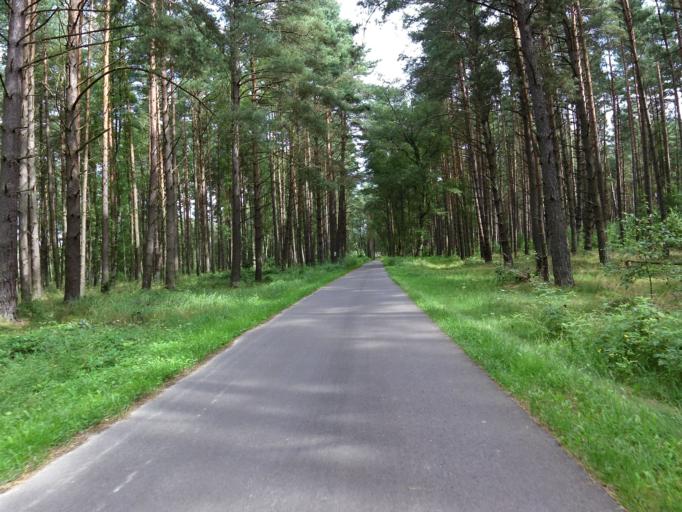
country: DE
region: Brandenburg
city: Lychen
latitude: 53.2681
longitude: 13.3051
